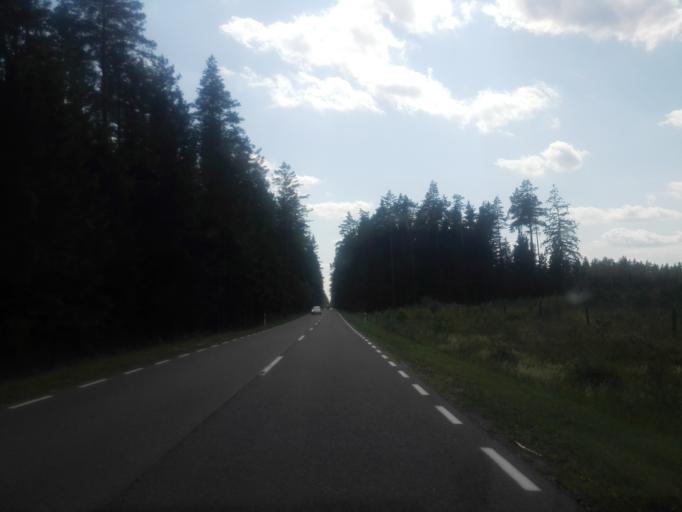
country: PL
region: Podlasie
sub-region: Powiat sejnenski
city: Krasnopol
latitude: 53.9280
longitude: 23.1600
